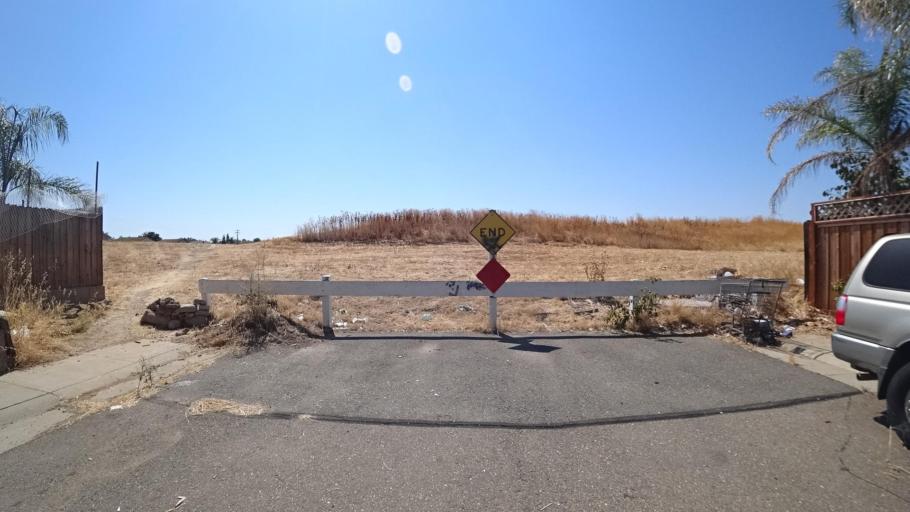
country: US
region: California
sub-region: Sacramento County
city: Laguna
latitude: 38.4416
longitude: -121.3960
